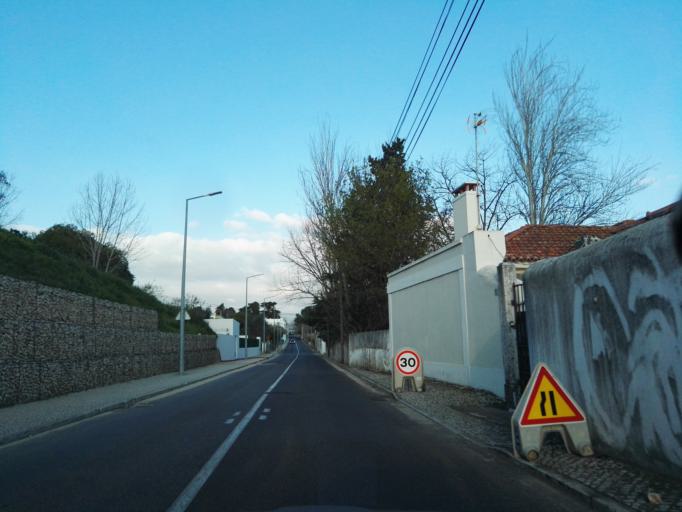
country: PT
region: Lisbon
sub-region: Vila Franca de Xira
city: Povoa de Santa Iria
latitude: 38.8566
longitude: -9.0689
